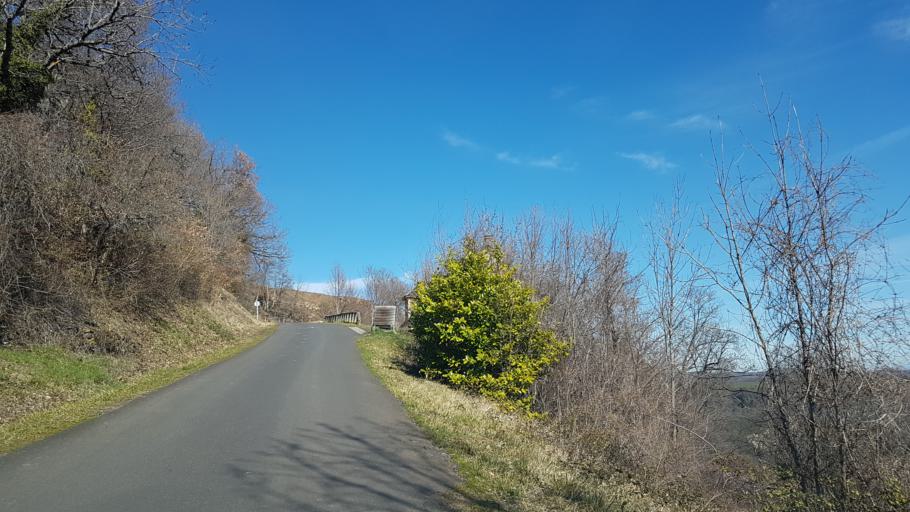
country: FR
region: Auvergne
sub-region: Departement du Puy-de-Dome
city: Aydat
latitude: 45.5396
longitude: 2.9916
